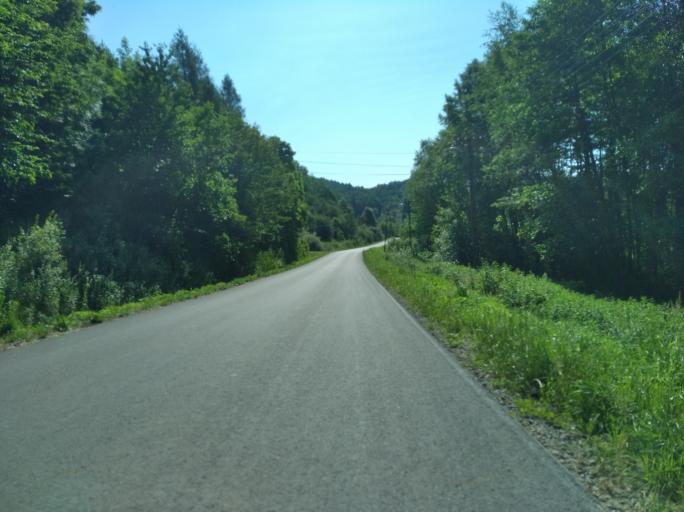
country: PL
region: Subcarpathian Voivodeship
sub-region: Powiat brzozowski
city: Wesola
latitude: 49.8263
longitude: 22.1600
